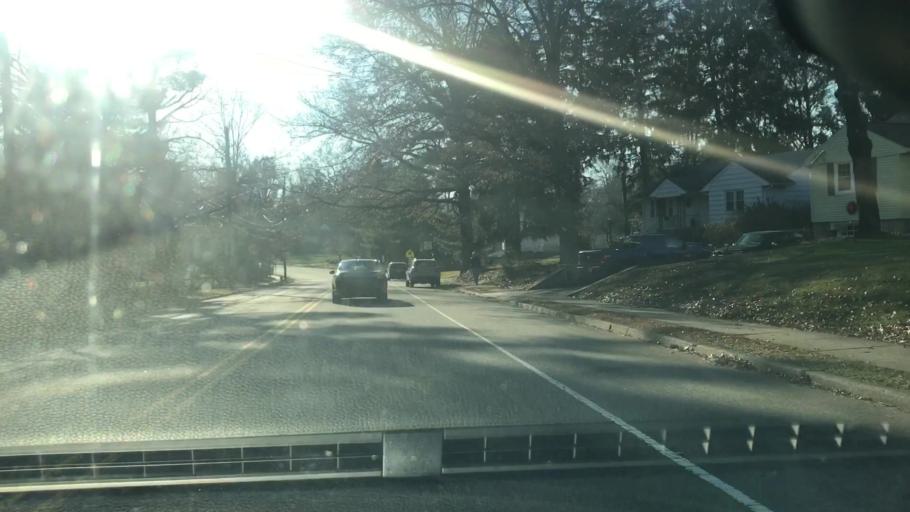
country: US
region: New Jersey
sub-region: Essex County
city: Cedar Grove
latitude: 40.8502
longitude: -74.2215
